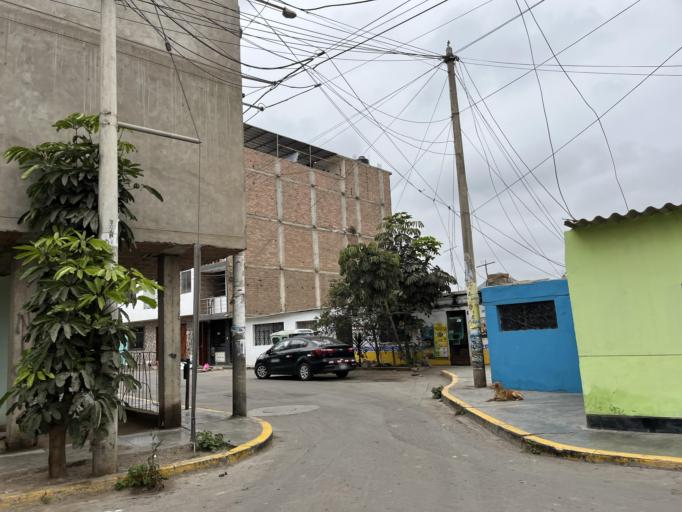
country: PE
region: La Libertad
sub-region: Provincia de Trujillo
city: Trujillo
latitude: -8.1142
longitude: -79.0048
